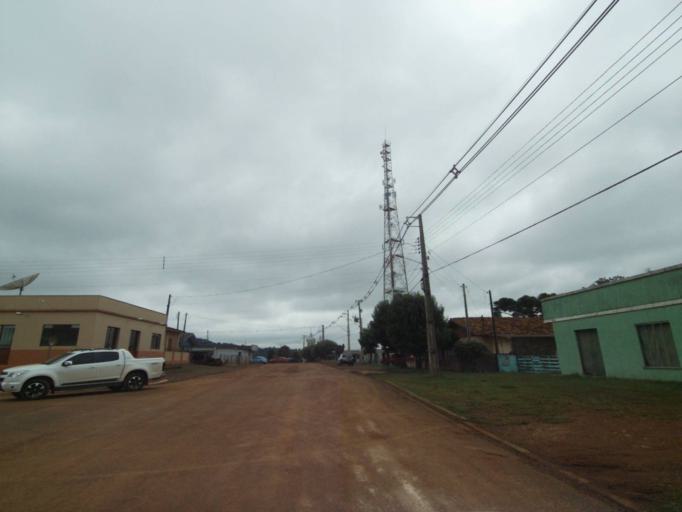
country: BR
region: Parana
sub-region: Pitanga
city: Pitanga
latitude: -24.9408
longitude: -51.8730
